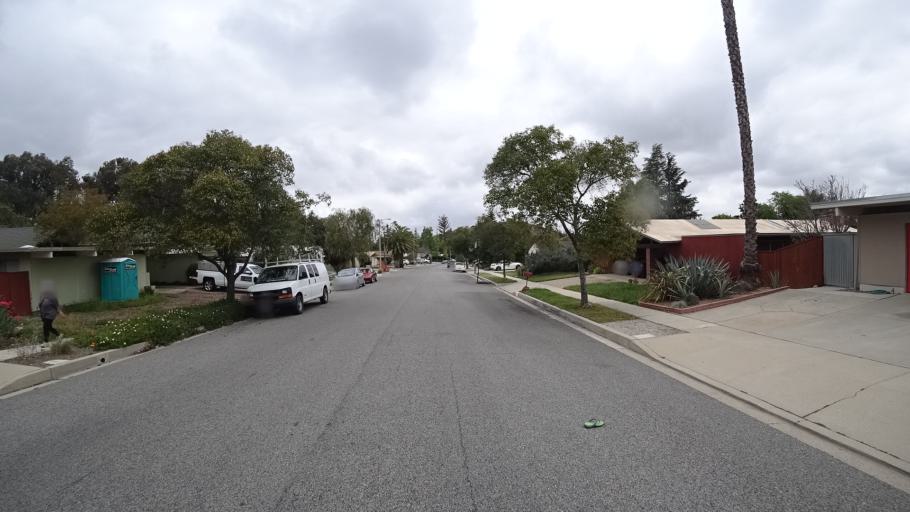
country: US
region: California
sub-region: Ventura County
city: Casa Conejo
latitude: 34.2016
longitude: -118.8896
